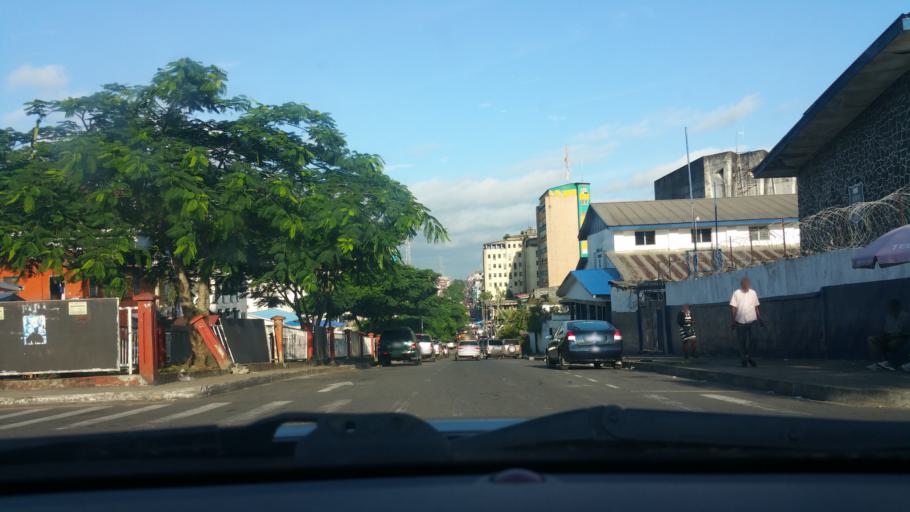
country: LR
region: Montserrado
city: Monrovia
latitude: 6.3184
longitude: -10.8099
